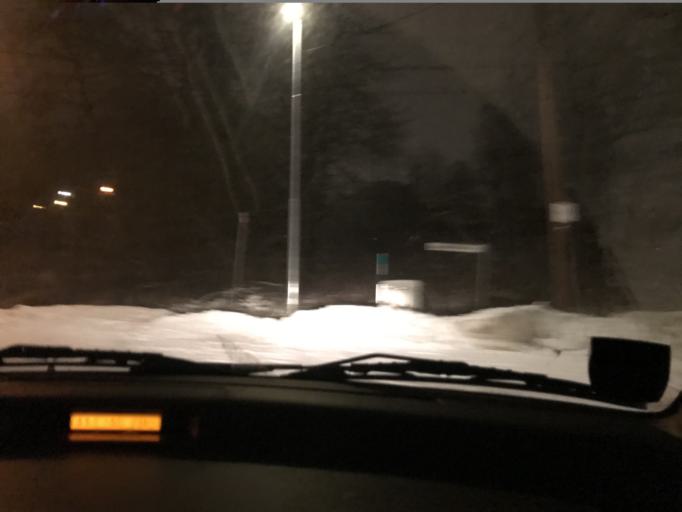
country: SE
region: Stockholm
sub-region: Nacka Kommun
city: Fisksatra
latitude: 59.3137
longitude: 18.2450
